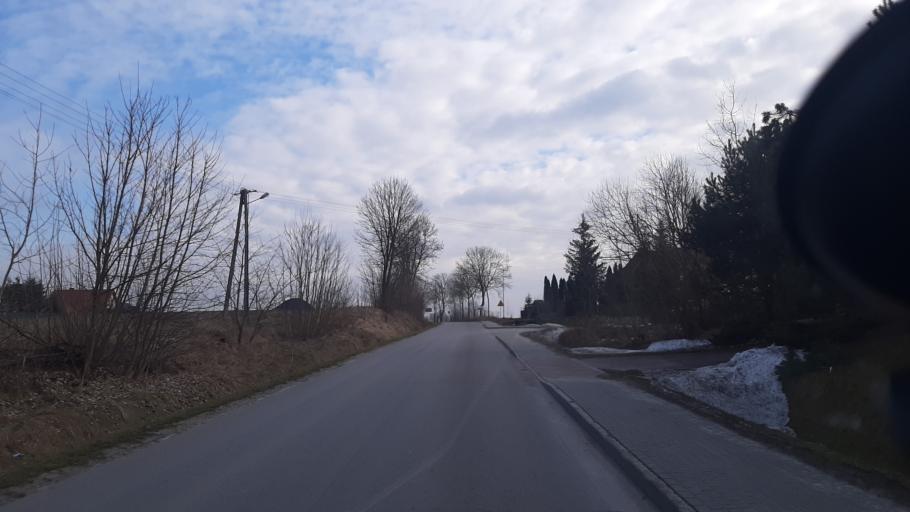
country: PL
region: Lublin Voivodeship
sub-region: Powiat lubartowski
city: Ostrow Lubelski
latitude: 51.4887
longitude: 22.8664
